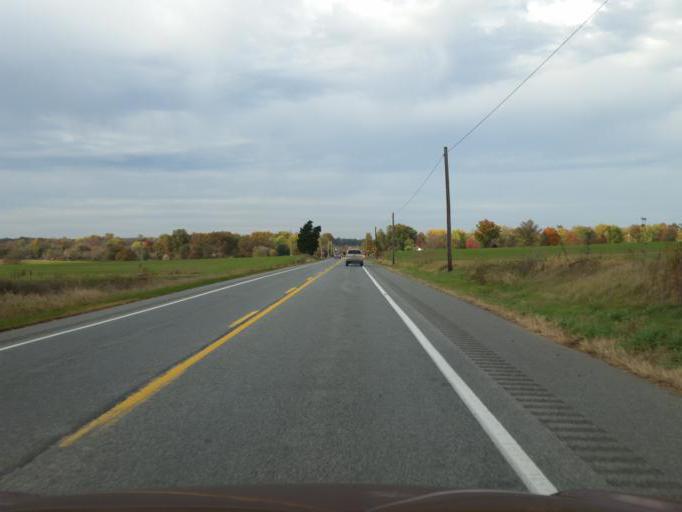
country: US
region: Pennsylvania
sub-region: Lancaster County
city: Elizabethtown
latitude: 40.1939
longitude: -76.6066
